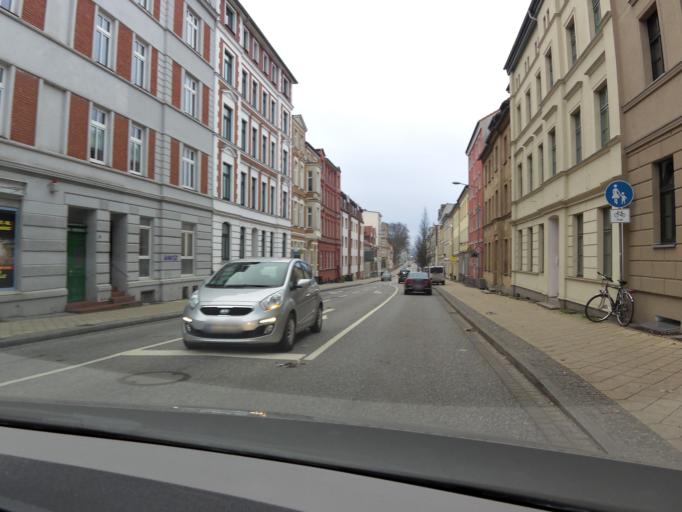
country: DE
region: Mecklenburg-Vorpommern
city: Werdervorstadt
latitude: 53.6372
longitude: 11.4233
